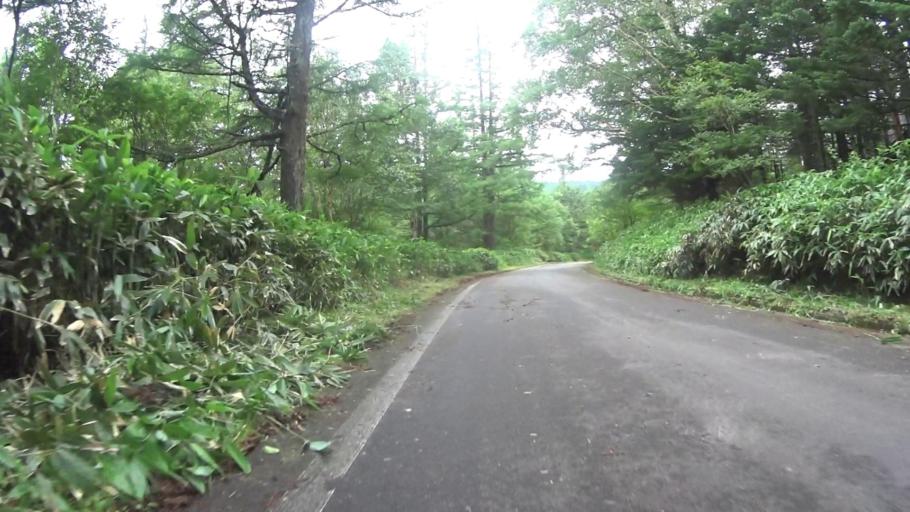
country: JP
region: Nagano
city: Saku
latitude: 36.1164
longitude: 138.3321
